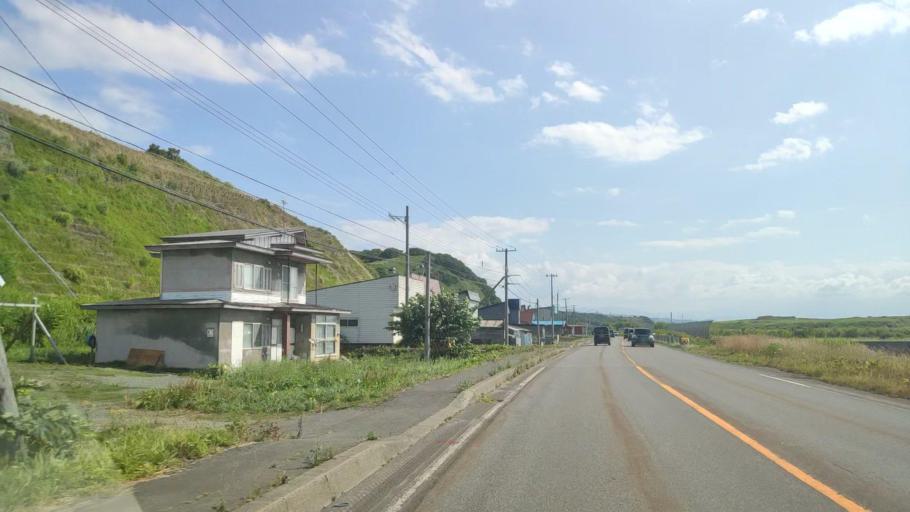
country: JP
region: Hokkaido
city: Rumoi
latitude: 43.9769
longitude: 141.6466
